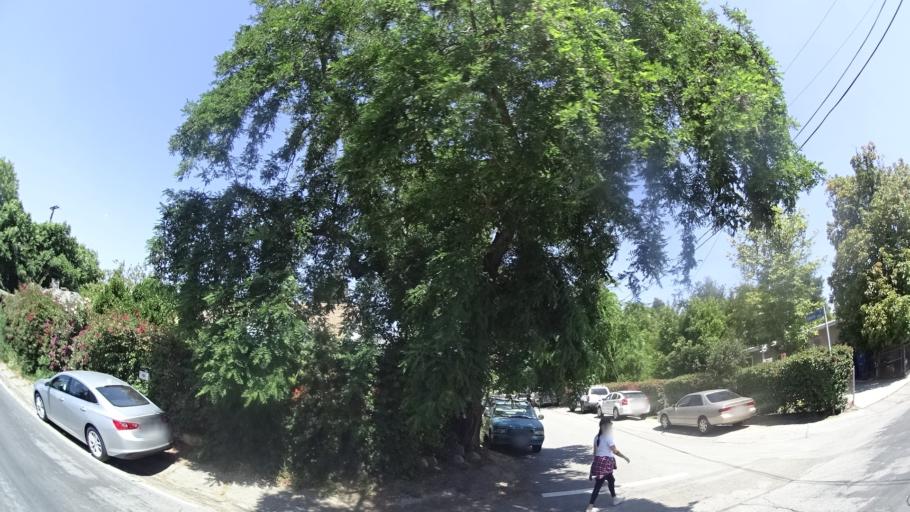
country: US
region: California
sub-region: Los Angeles County
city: Burbank
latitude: 34.2642
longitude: -118.3159
